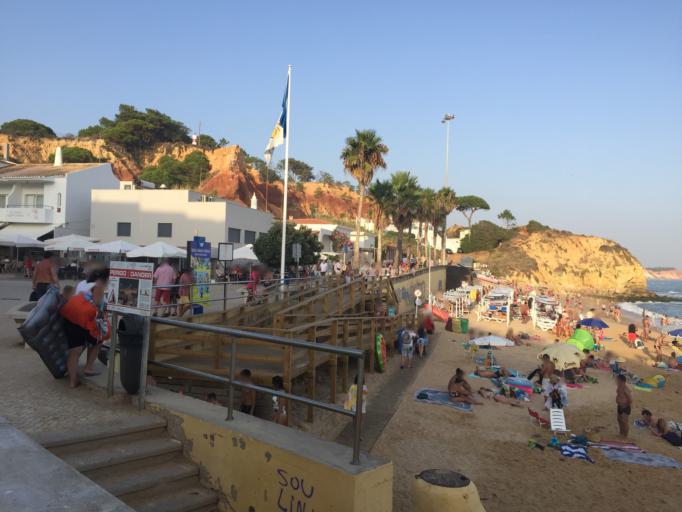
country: PT
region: Faro
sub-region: Loule
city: Boliqueime
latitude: 37.0899
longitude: -8.1907
